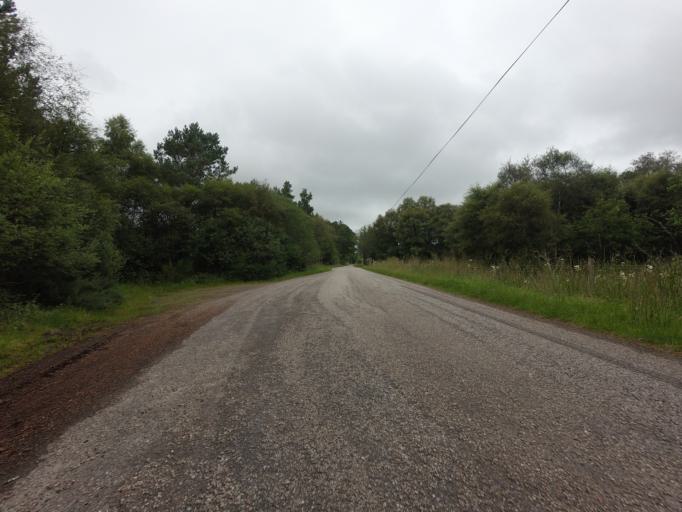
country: GB
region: Scotland
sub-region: Highland
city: Alness
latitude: 57.9905
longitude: -4.4112
